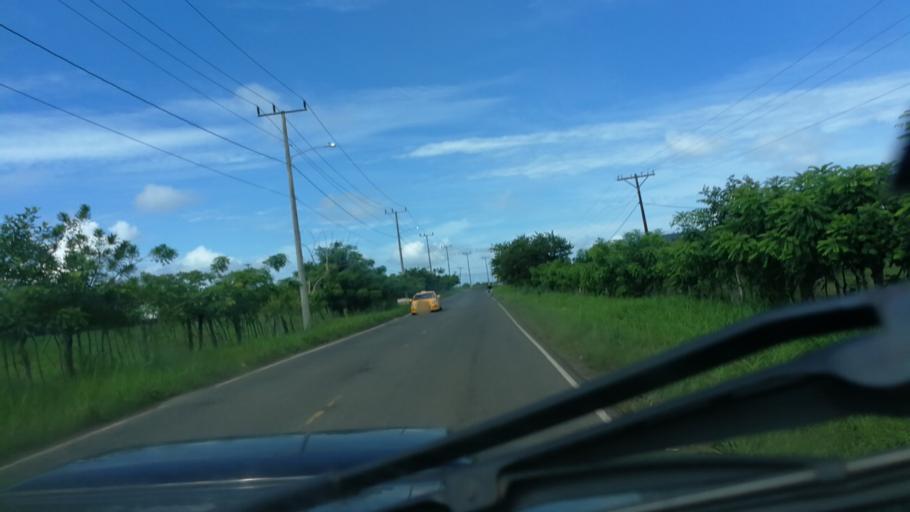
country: PA
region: Panama
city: Los Lotes
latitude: 9.1064
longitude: -79.2700
